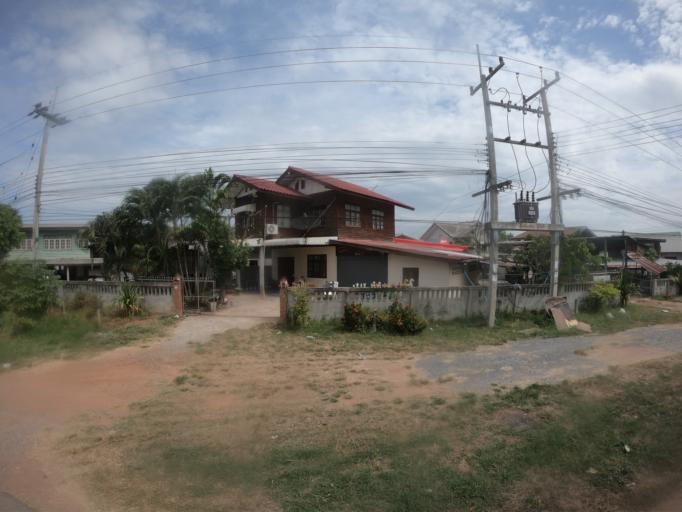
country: TH
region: Maha Sarakham
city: Chiang Yuen
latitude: 16.3664
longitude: 103.1061
